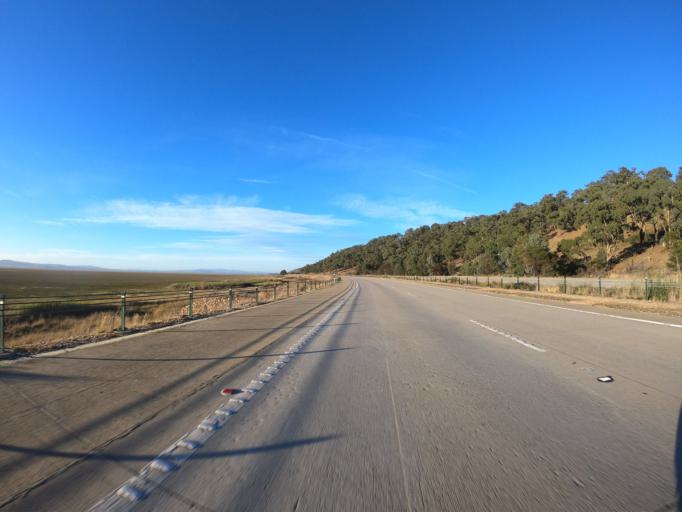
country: AU
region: New South Wales
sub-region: Yass Valley
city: Gundaroo
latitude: -35.0874
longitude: 149.3747
